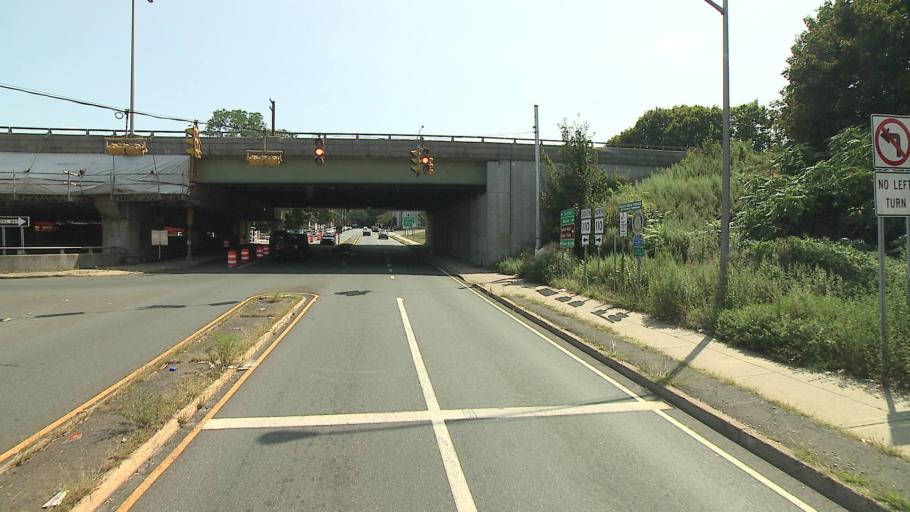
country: US
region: Connecticut
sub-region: Fairfield County
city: Shelton
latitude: 41.3128
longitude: -73.0892
